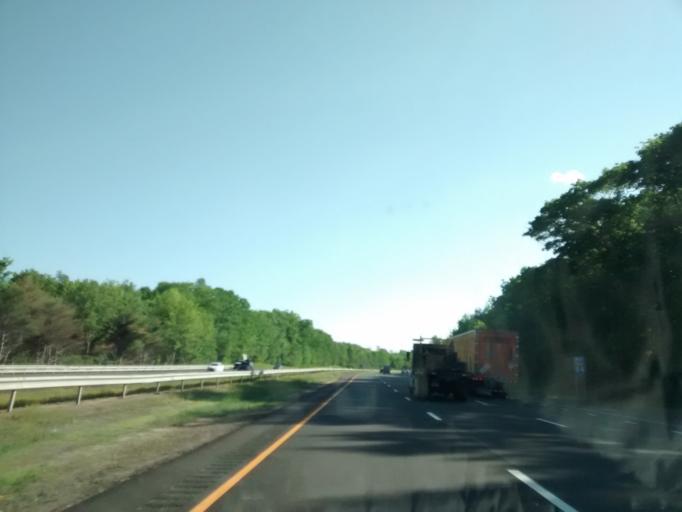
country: US
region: Connecticut
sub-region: Tolland County
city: Stafford
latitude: 41.9533
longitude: -72.2001
